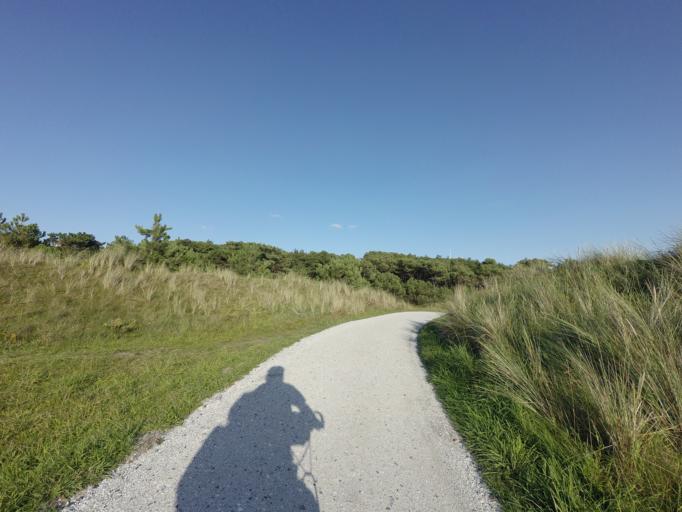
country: NL
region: Friesland
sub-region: Gemeente Terschelling
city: West-Terschelling
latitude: 53.3592
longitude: 5.2079
